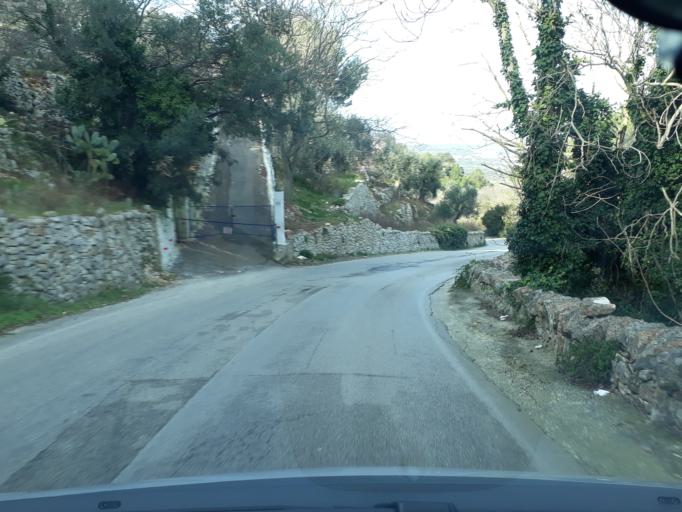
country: IT
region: Apulia
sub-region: Provincia di Brindisi
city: Lamie di Olimpie-Selva
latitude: 40.8021
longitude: 17.3524
